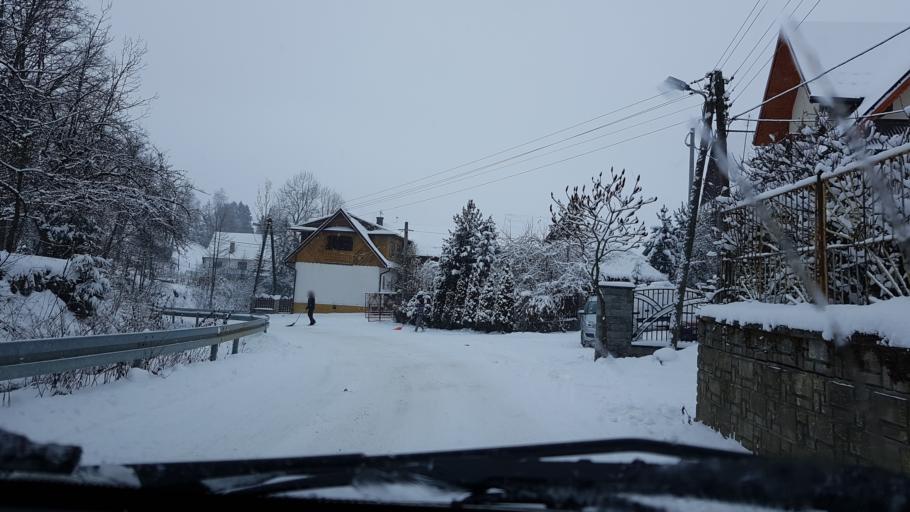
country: PL
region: Lesser Poland Voivodeship
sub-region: Powiat tatrzanski
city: Czarna Gora
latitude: 49.3552
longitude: 20.1520
